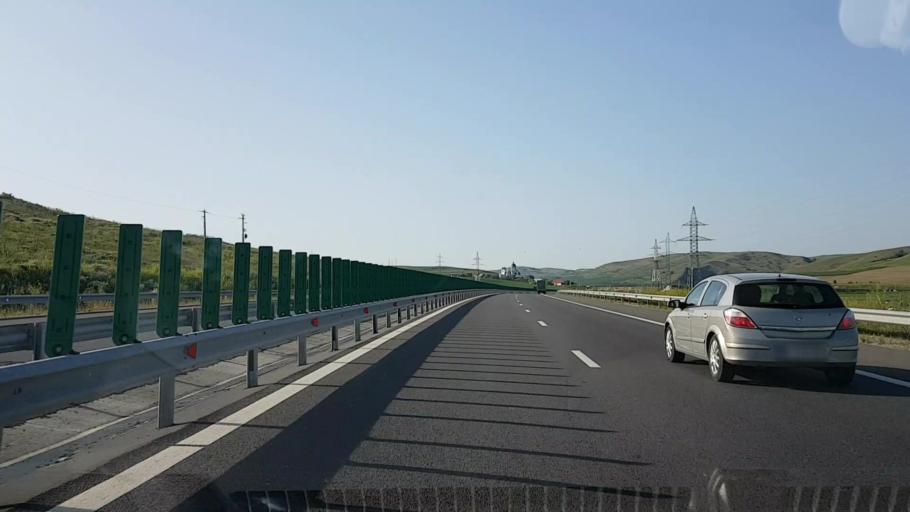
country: RO
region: Alba
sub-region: Comuna Unirea
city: Unirea
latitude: 46.4256
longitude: 23.7975
